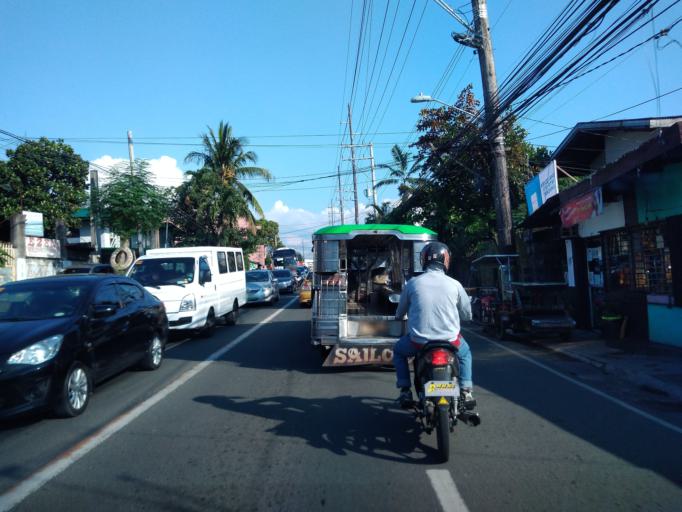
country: PH
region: Calabarzon
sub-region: Province of Laguna
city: Los Banos
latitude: 14.1810
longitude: 121.2334
